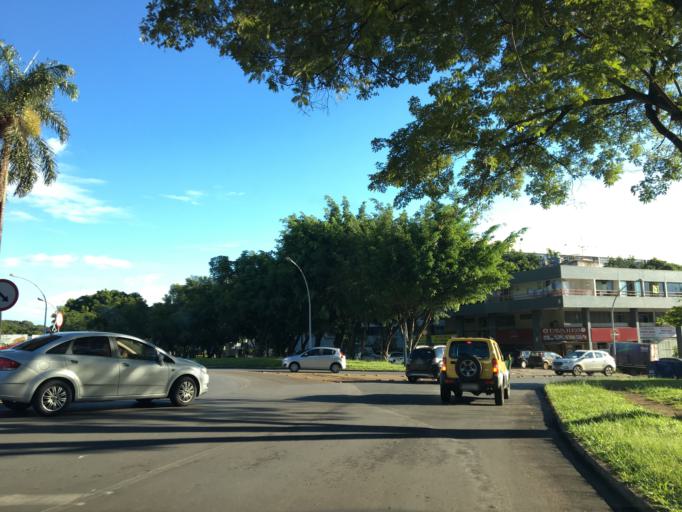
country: BR
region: Federal District
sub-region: Brasilia
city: Brasilia
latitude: -15.7470
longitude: -47.8927
